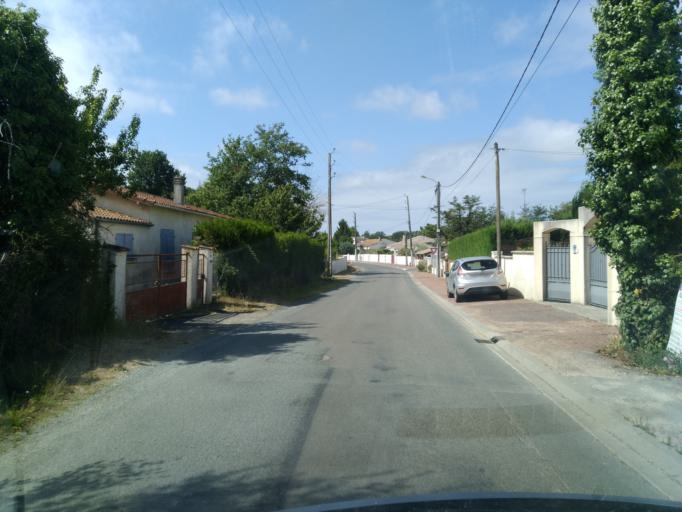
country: FR
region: Poitou-Charentes
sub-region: Departement de la Charente-Maritime
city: Breuillet
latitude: 45.6968
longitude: -1.0658
